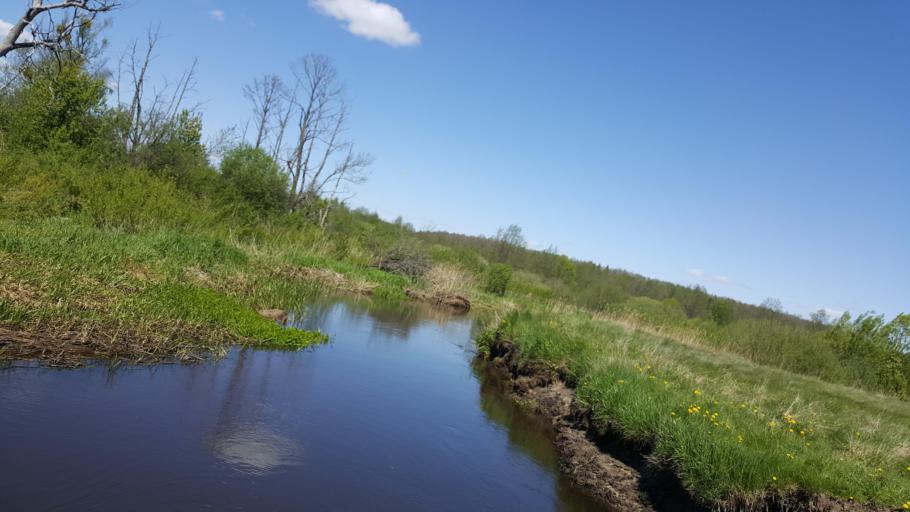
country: BY
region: Brest
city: Kamyanyuki
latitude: 52.5588
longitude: 23.8137
